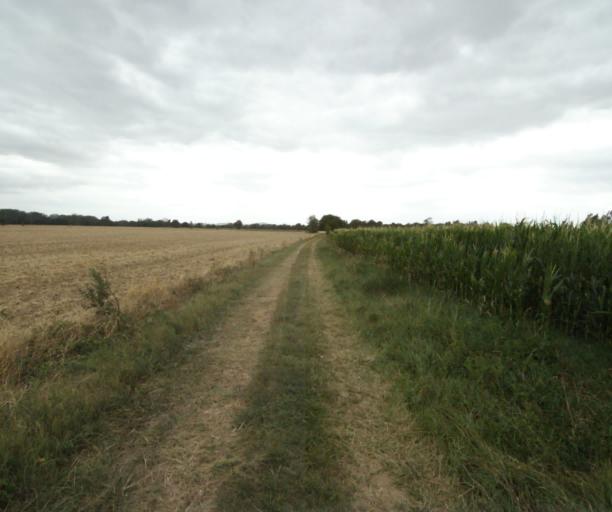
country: FR
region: Midi-Pyrenees
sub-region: Departement du Tarn
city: Soreze
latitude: 43.4613
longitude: 2.0461
